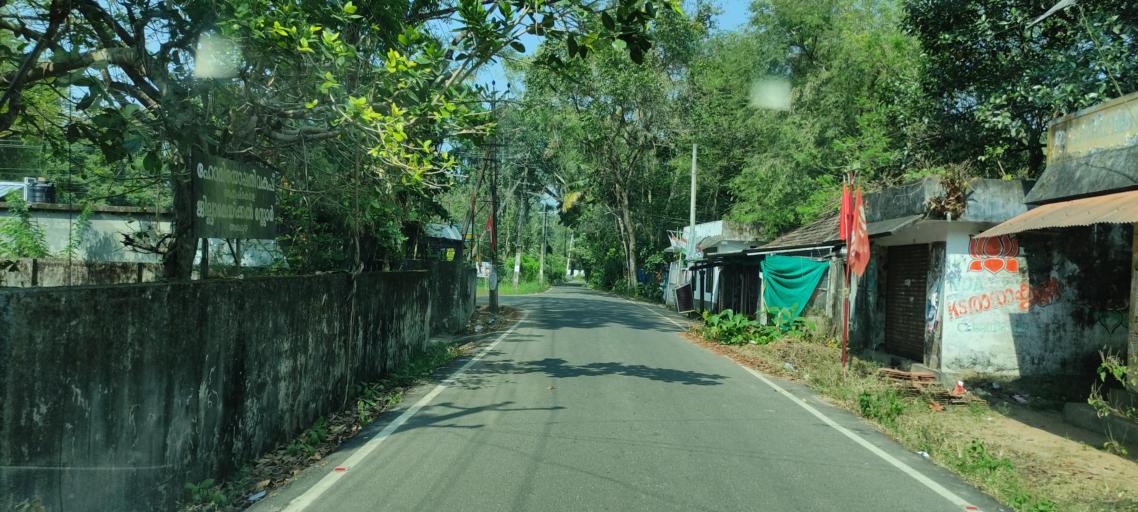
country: IN
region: Kerala
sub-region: Alappuzha
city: Alleppey
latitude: 9.5550
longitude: 76.3180
